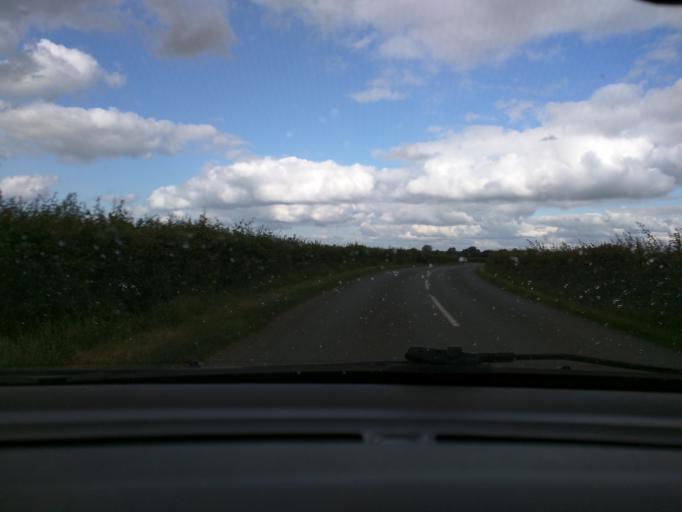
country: GB
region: England
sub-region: Suffolk
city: Framlingham
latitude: 52.2224
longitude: 1.3618
